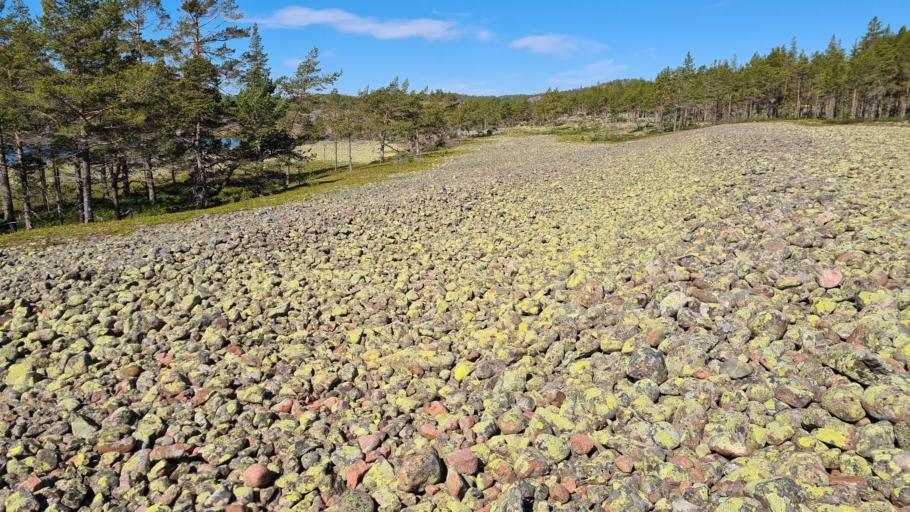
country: SE
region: Vaesternorrland
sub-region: OErnskoeldsviks Kommun
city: Kopmanholmen
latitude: 62.9630
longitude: 18.5367
